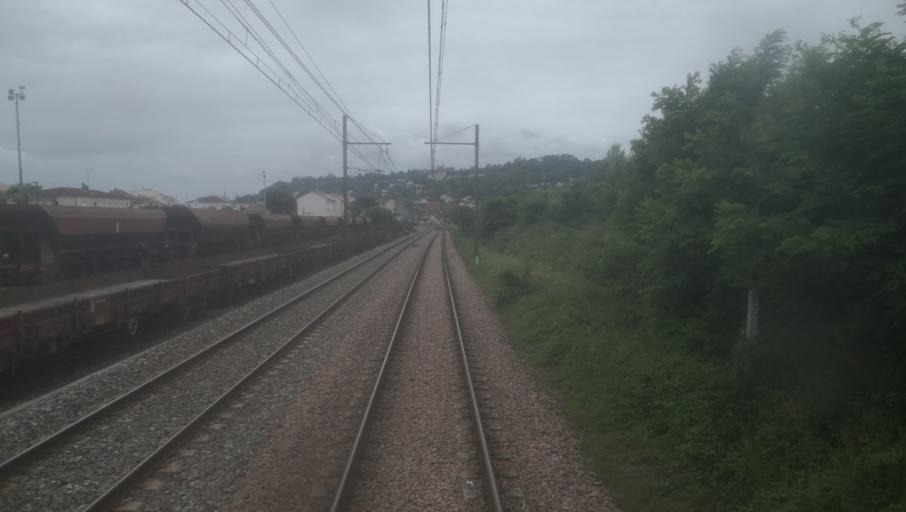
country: FR
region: Aquitaine
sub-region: Departement du Lot-et-Garonne
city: Agen
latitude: 44.2040
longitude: 0.6345
